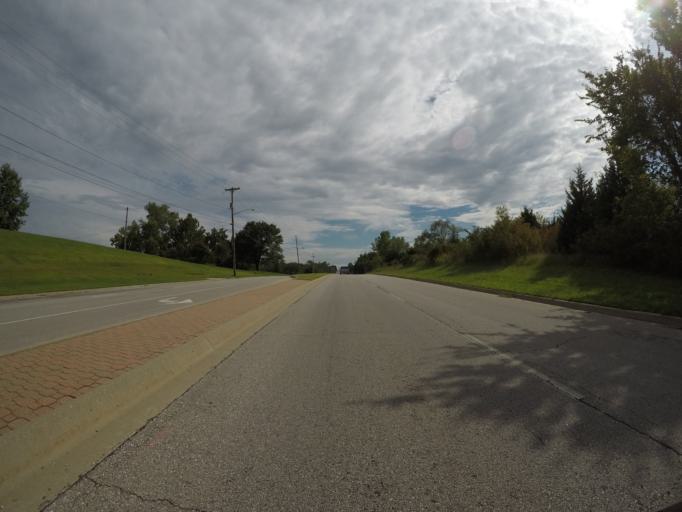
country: US
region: Kansas
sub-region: Wyandotte County
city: Edwardsville
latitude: 39.1426
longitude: -94.8083
